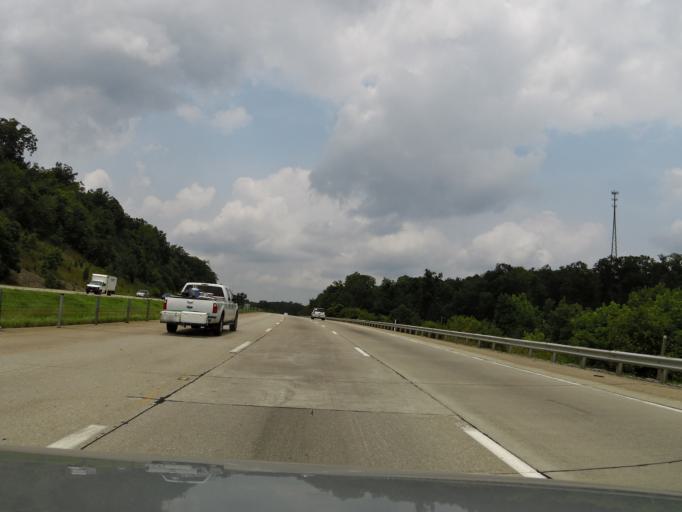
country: US
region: Kentucky
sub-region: Bullitt County
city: Shepherdsville
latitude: 37.9557
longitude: -85.6905
